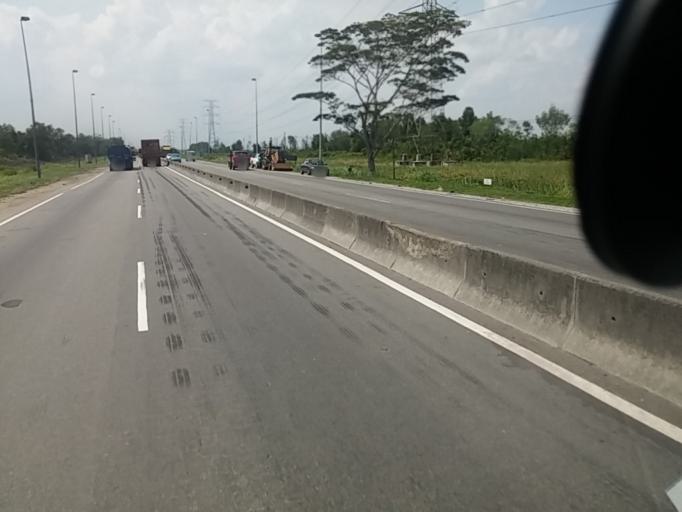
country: MY
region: Selangor
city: Klang
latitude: 2.9722
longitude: 101.3654
